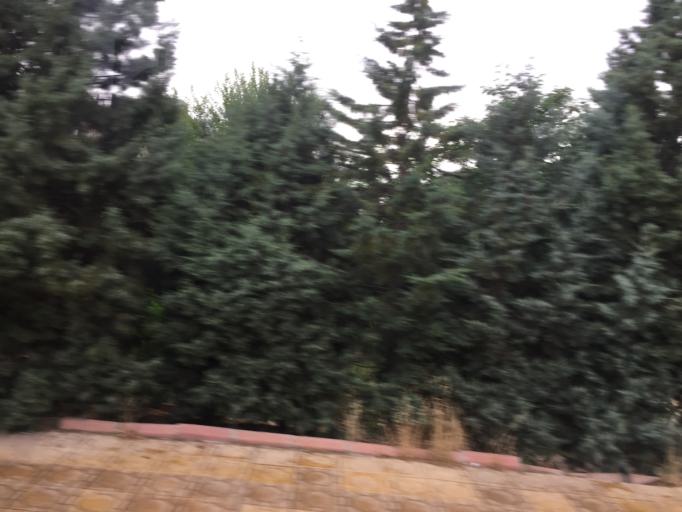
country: TR
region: Gaziantep
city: Gaziantep
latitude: 37.0734
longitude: 37.3722
